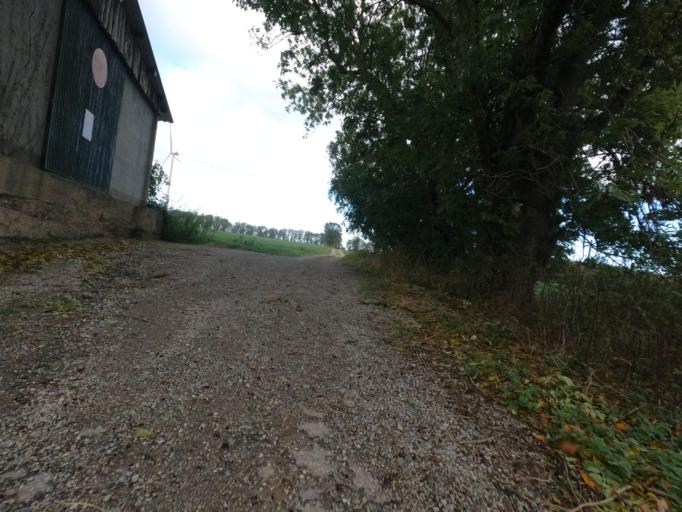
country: DE
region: North Rhine-Westphalia
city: Huckelhoven
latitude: 51.0592
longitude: 6.2557
